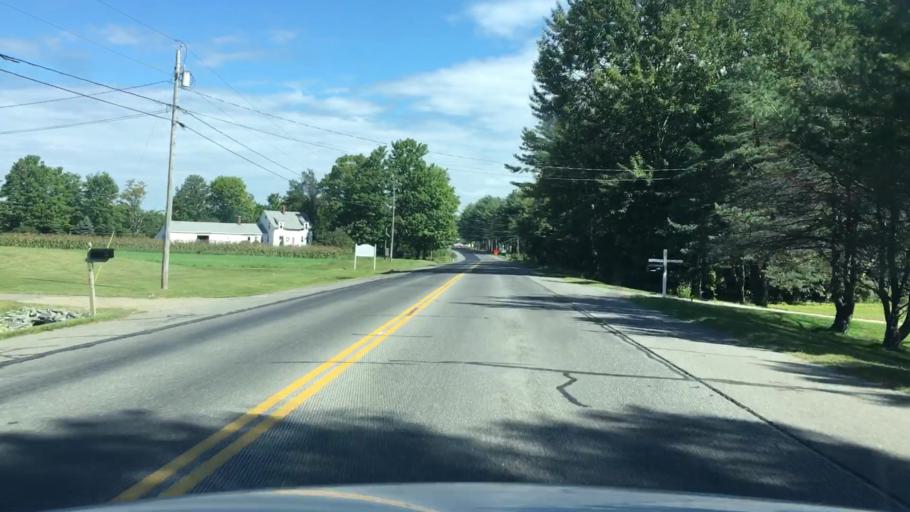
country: US
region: Maine
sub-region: Penobscot County
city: Corinna
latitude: 44.8990
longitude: -69.2676
